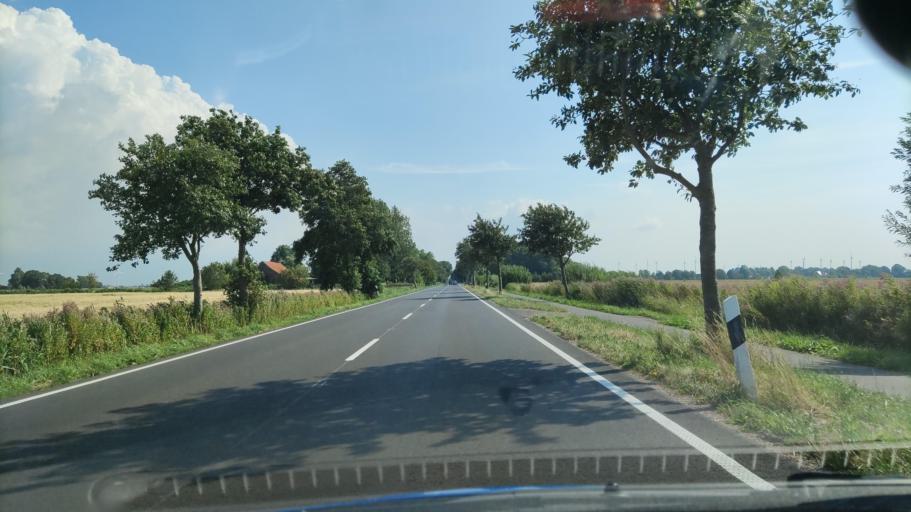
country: DE
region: Lower Saxony
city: Werdum
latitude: 53.6636
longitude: 7.7897
